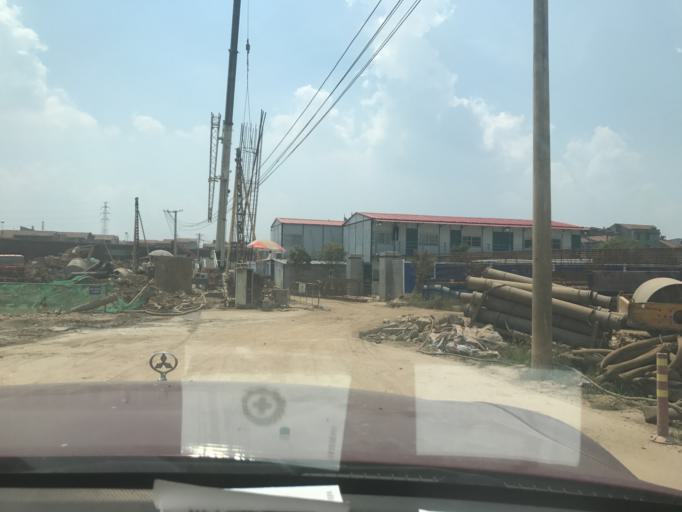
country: CN
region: Hubei
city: Zhanjiaji
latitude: 30.6906
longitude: 114.3395
